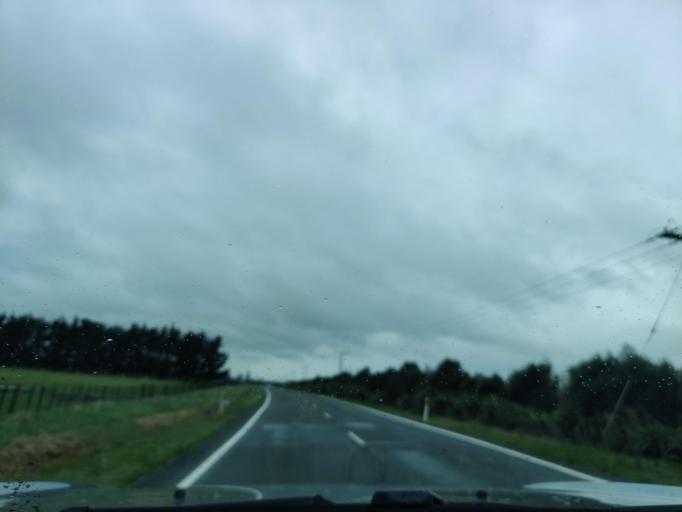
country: NZ
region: Hawke's Bay
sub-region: Hastings District
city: Hastings
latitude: -40.0065
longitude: 176.3876
